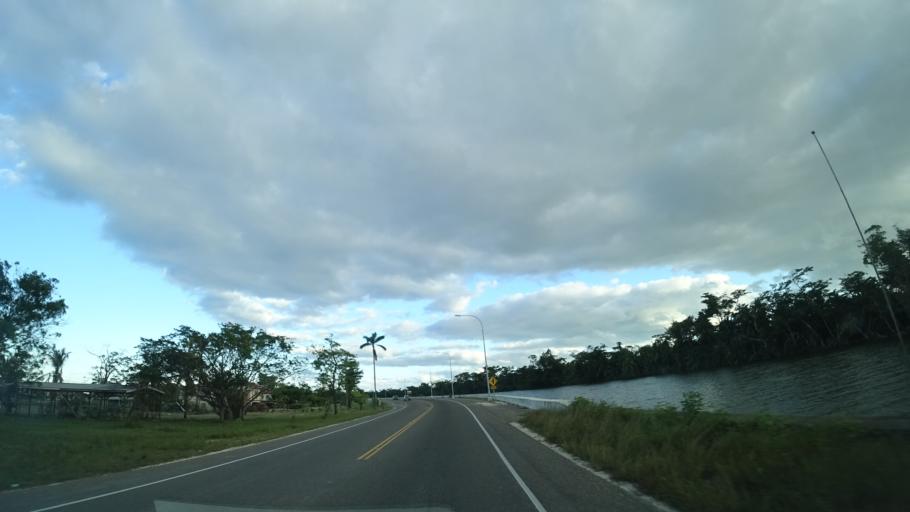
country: BZ
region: Belize
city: Belize City
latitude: 17.5438
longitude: -88.2666
